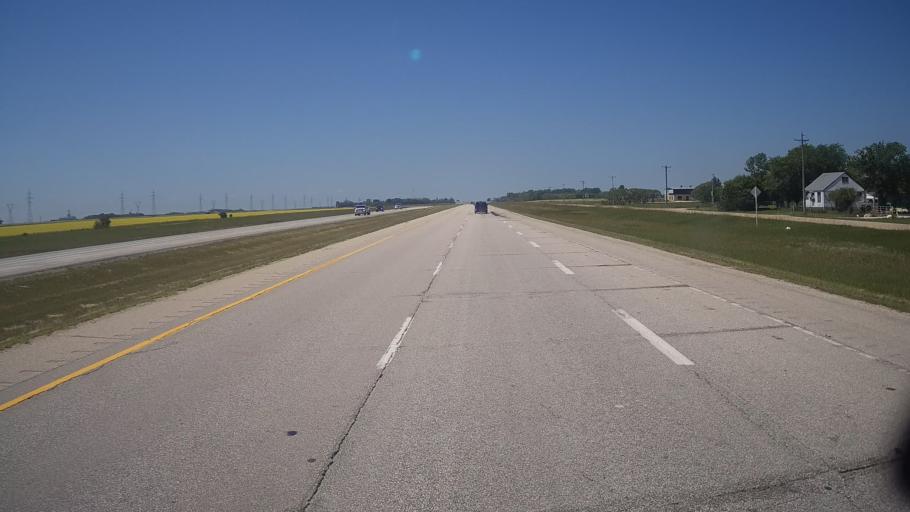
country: CA
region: Manitoba
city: Winnipeg
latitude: 49.9900
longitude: -97.2423
